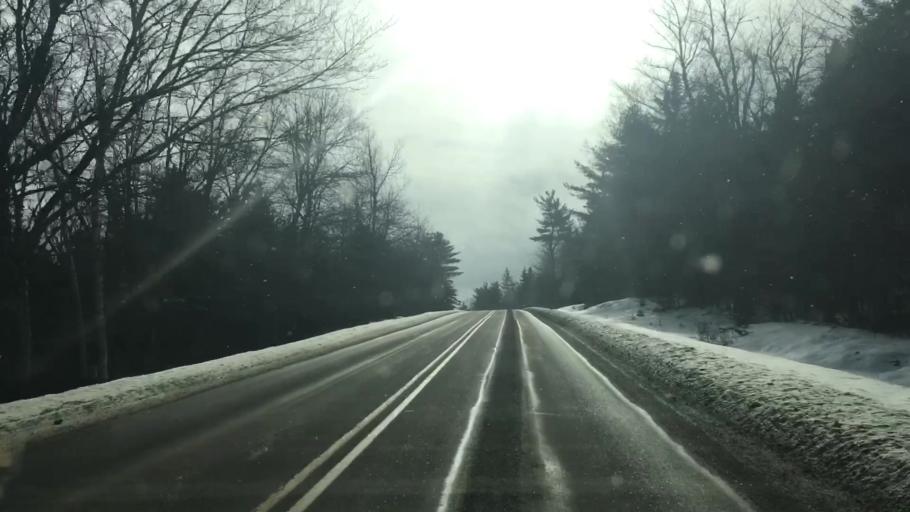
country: US
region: Maine
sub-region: Washington County
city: Calais
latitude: 45.0666
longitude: -67.3304
